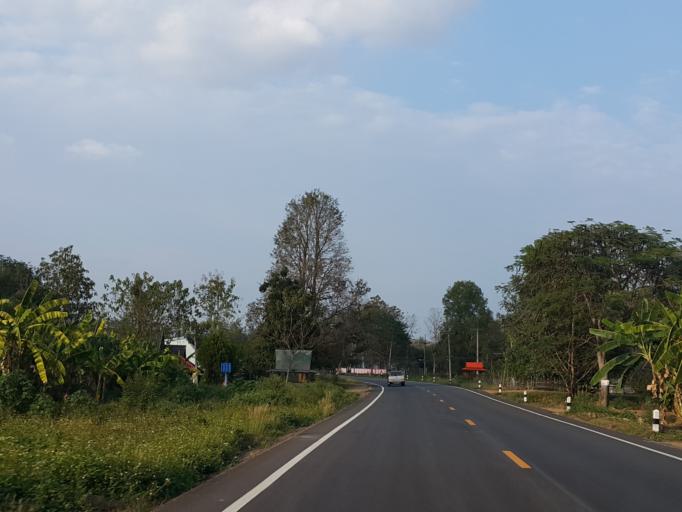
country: TH
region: Lampang
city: Lampang
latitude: 18.4829
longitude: 99.4716
